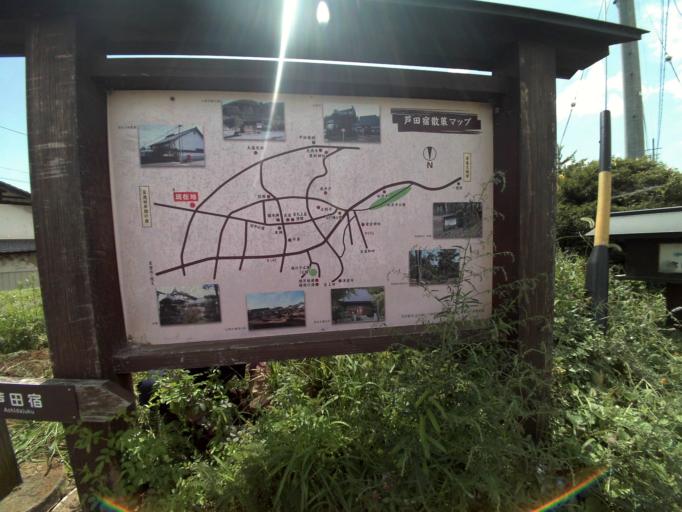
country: JP
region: Nagano
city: Kamimaruko
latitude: 36.2722
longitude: 138.3209
